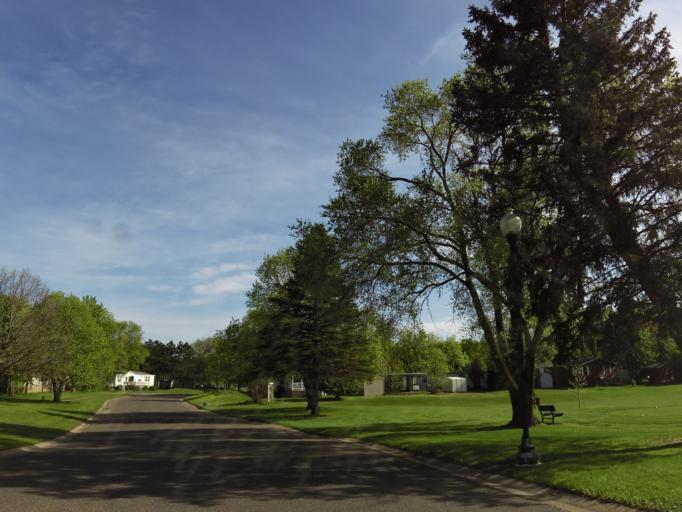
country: US
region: Minnesota
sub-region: Washington County
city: Lake Elmo
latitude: 44.9609
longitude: -92.8806
